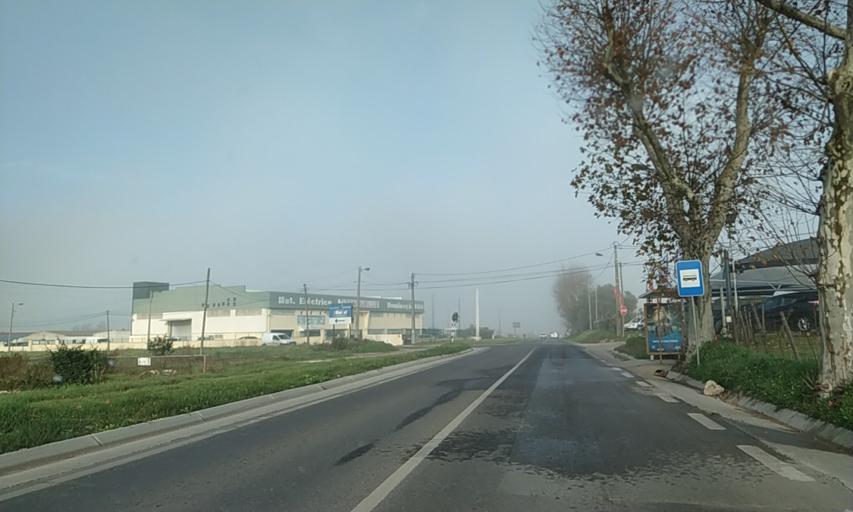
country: PT
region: Setubal
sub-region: Palmela
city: Pinhal Novo
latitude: 38.6721
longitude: -8.9321
